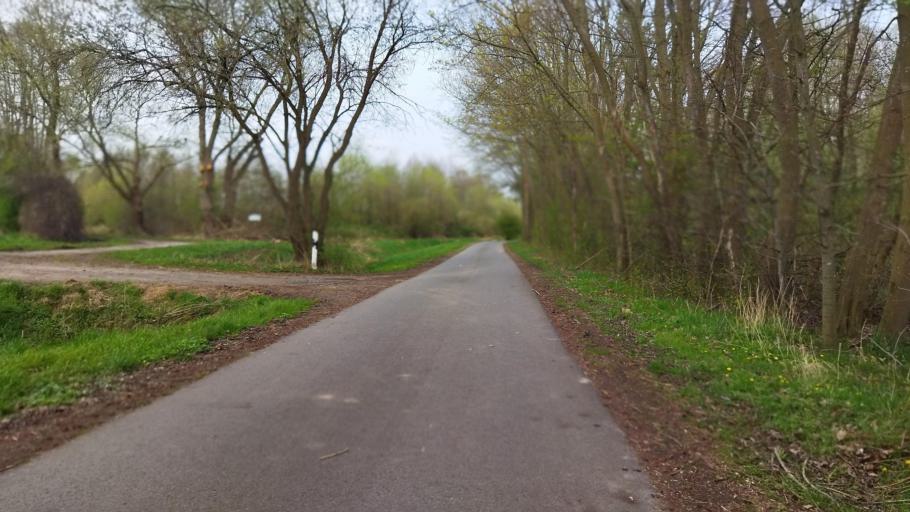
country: DE
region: Lower Saxony
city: Raddestorf
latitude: 52.4316
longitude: 8.9731
